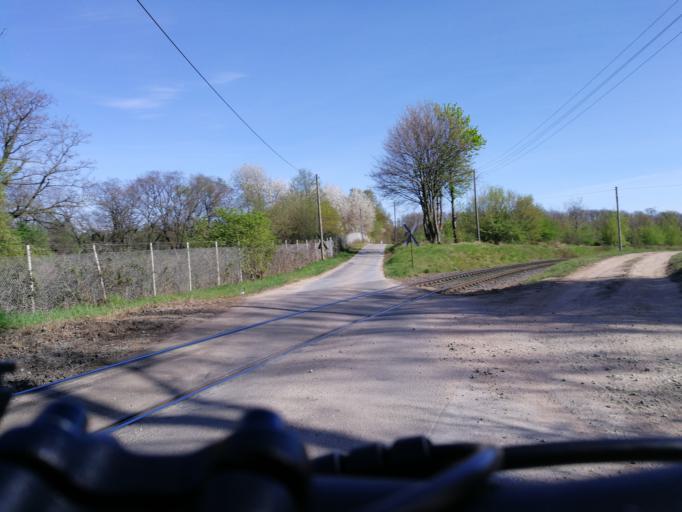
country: DE
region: North Rhine-Westphalia
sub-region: Regierungsbezirk Dusseldorf
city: Dormagen
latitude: 51.1448
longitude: 6.7787
